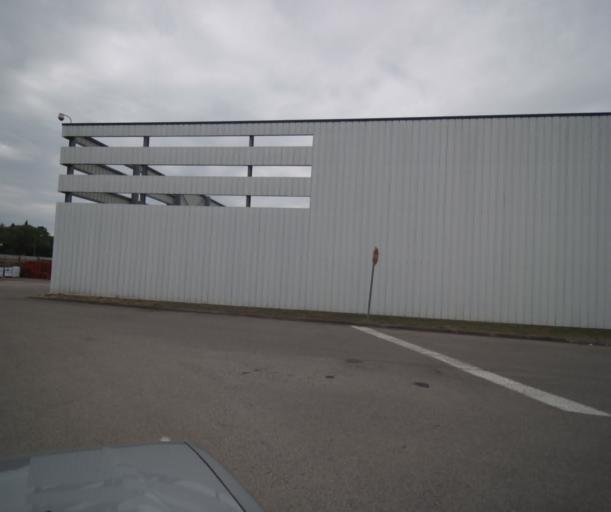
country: FR
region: Languedoc-Roussillon
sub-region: Departement de l'Aude
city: Limoux
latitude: 43.0743
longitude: 2.2237
